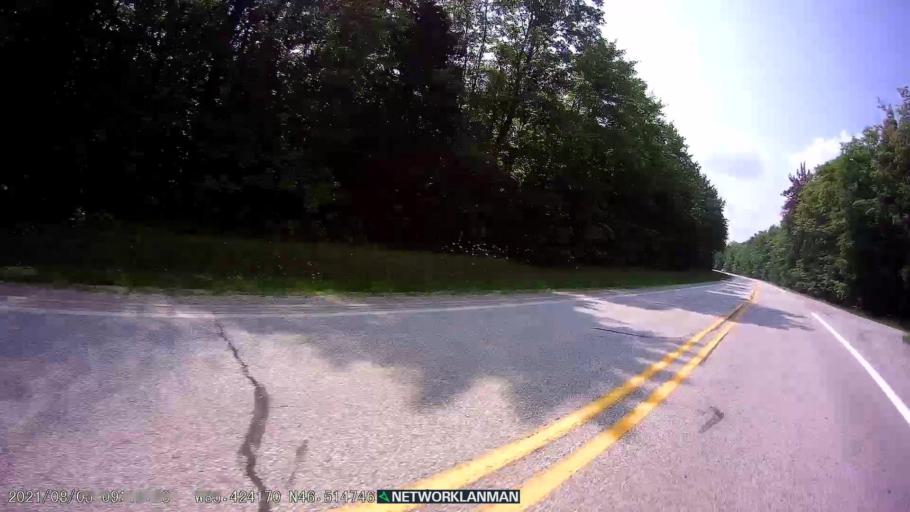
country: US
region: Michigan
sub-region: Luce County
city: Newberry
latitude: 46.5143
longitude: -85.4239
